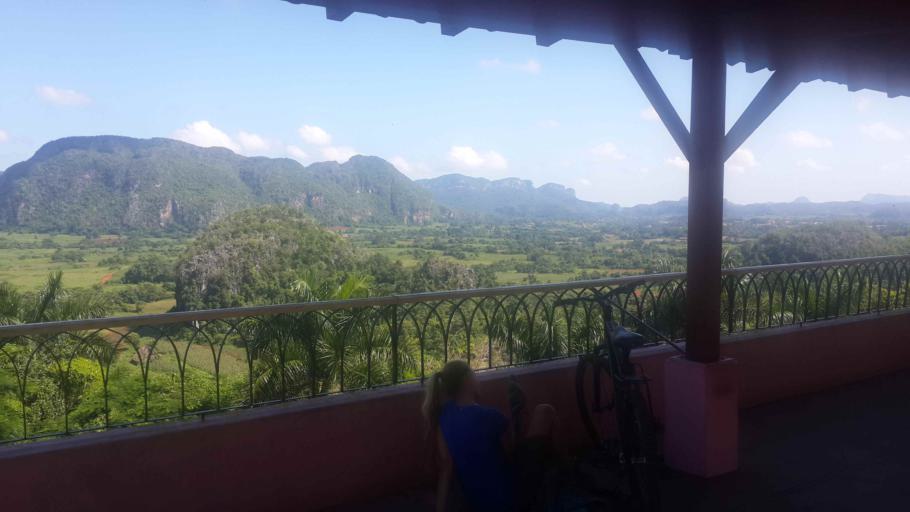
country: CU
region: Pinar del Rio
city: Vinales
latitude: 22.5963
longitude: -83.7237
